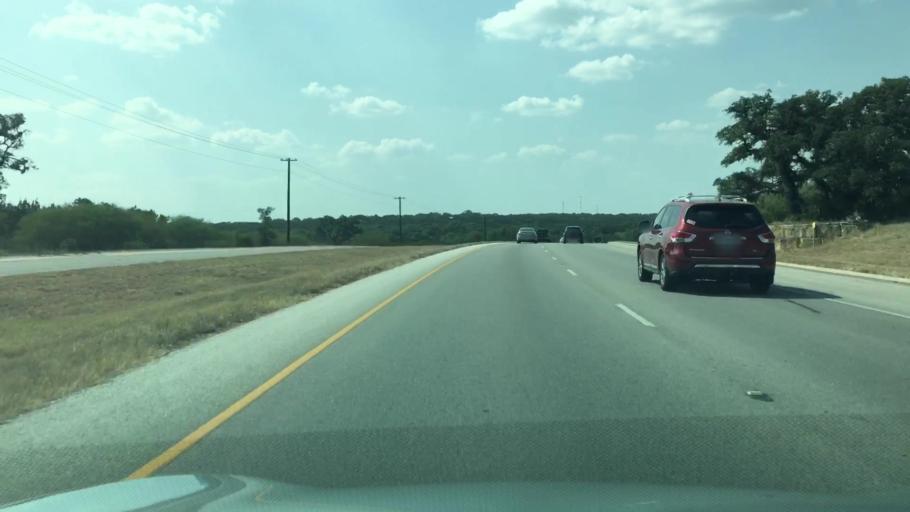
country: US
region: Texas
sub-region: Hays County
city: San Marcos
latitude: 29.8844
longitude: -97.9774
